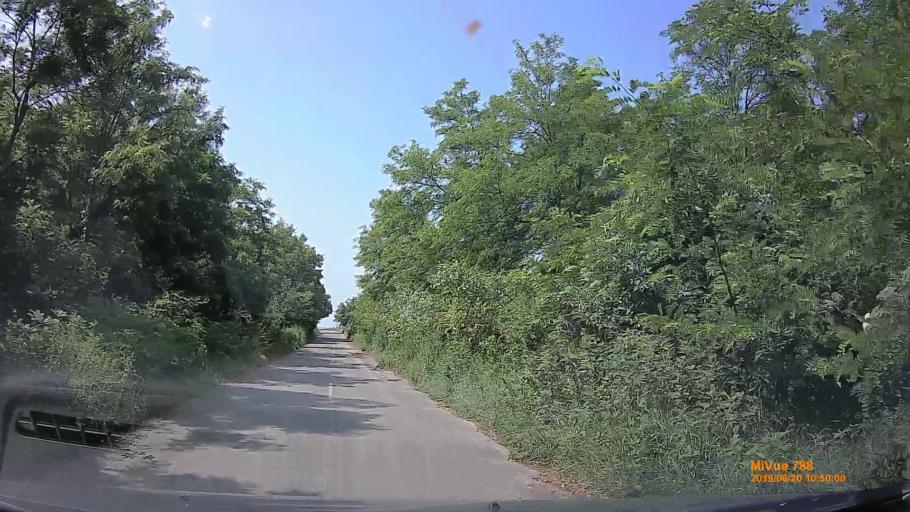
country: HU
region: Baranya
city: Mecseknadasd
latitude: 46.1596
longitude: 18.5824
